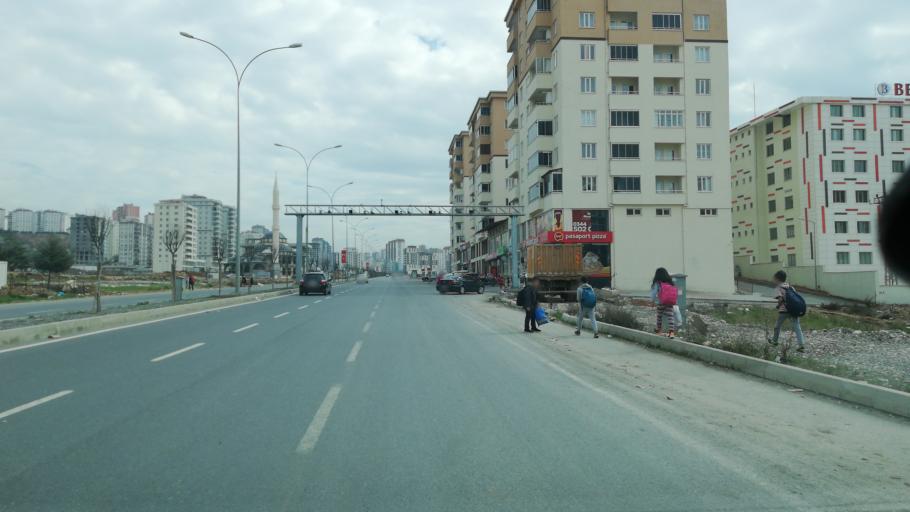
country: TR
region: Kahramanmaras
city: Kahramanmaras
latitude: 37.5900
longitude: 36.8391
